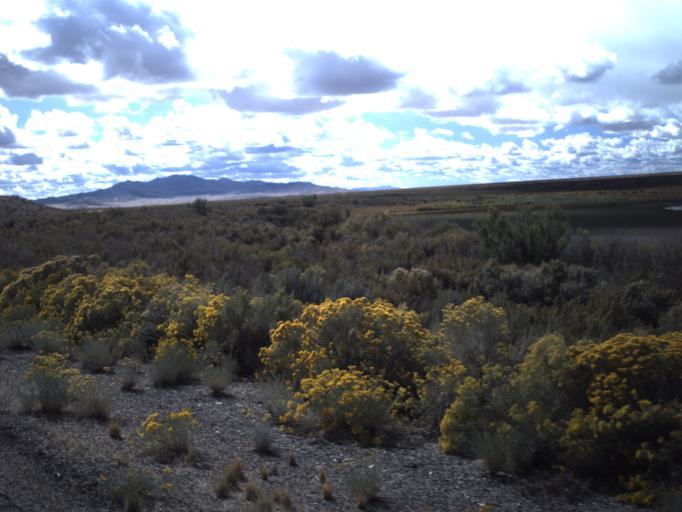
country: US
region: Nevada
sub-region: White Pine County
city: McGill
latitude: 38.8826
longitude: -114.0060
